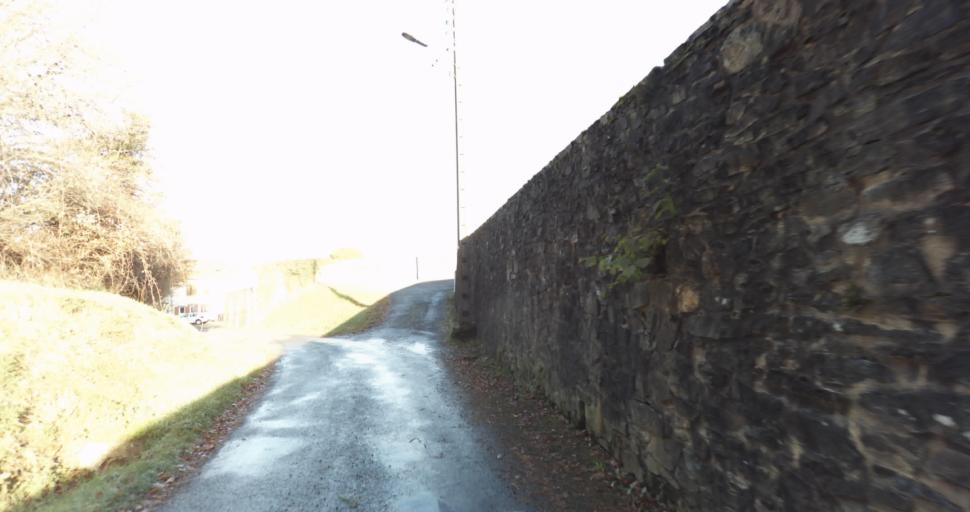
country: FR
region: Limousin
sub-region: Departement de la Haute-Vienne
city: Aixe-sur-Vienne
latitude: 45.7941
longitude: 1.1225
